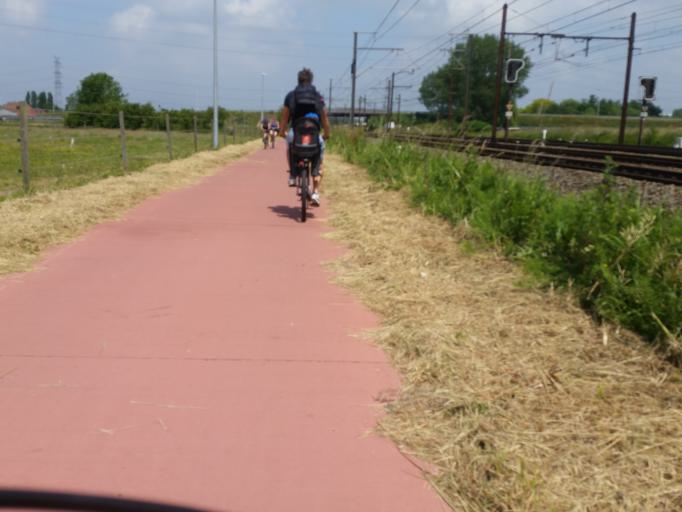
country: BE
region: Flanders
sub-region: Provincie Antwerpen
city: Lint
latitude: 51.1074
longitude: 4.4886
